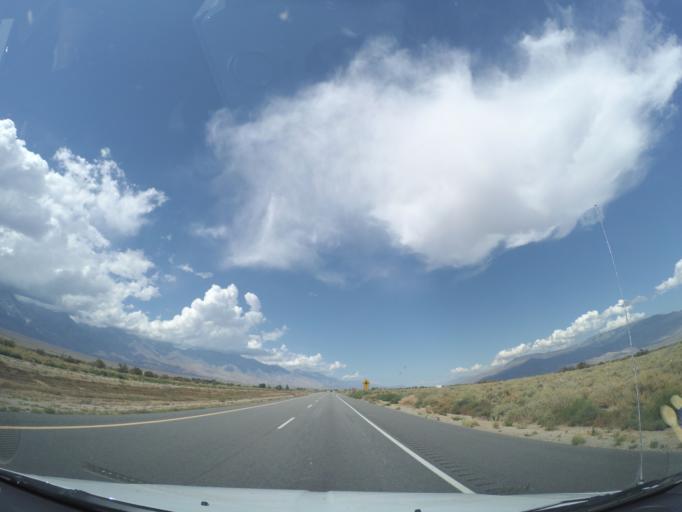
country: US
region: California
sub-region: Inyo County
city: Lone Pine
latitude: 36.7329
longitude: -118.1476
